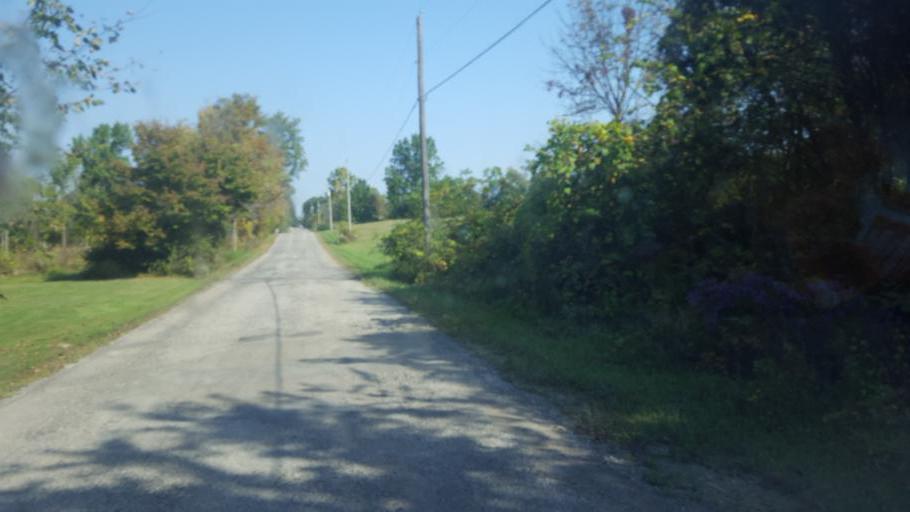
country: US
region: Ohio
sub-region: Crawford County
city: Galion
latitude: 40.6566
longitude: -82.7941
